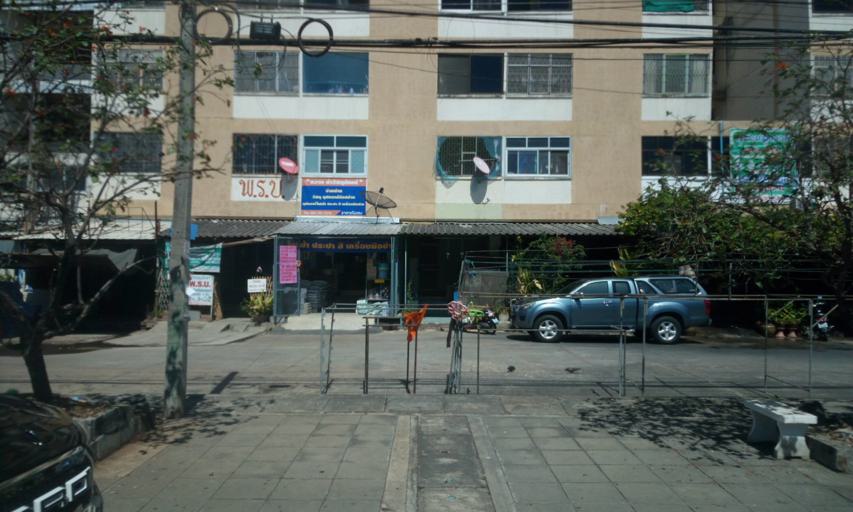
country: TH
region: Samut Prakan
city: Bang Bo District
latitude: 13.5592
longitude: 100.7654
